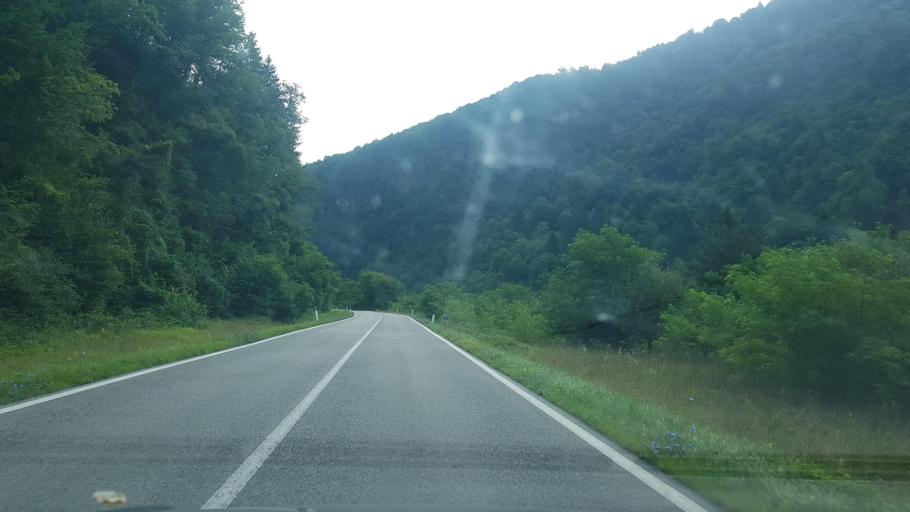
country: IT
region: Friuli Venezia Giulia
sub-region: Provincia di Udine
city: Zuglio
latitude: 46.4589
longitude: 13.0408
